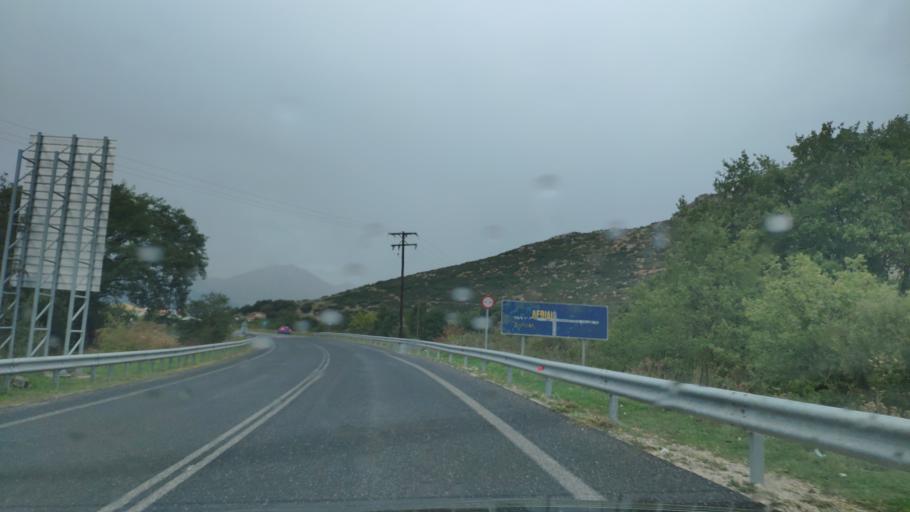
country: GR
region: Peloponnese
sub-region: Nomos Arkadias
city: Tripoli
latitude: 37.5947
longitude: 22.4345
